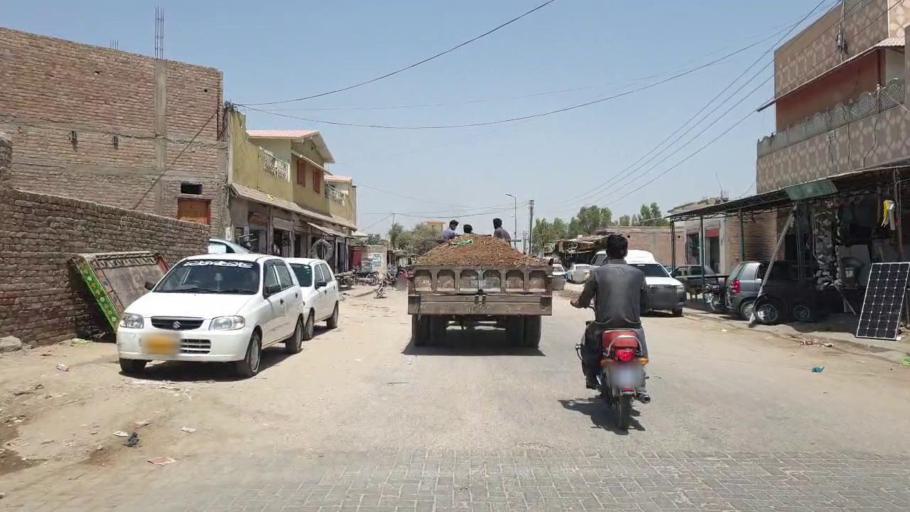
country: PK
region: Sindh
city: Adilpur
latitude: 27.9384
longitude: 69.3196
